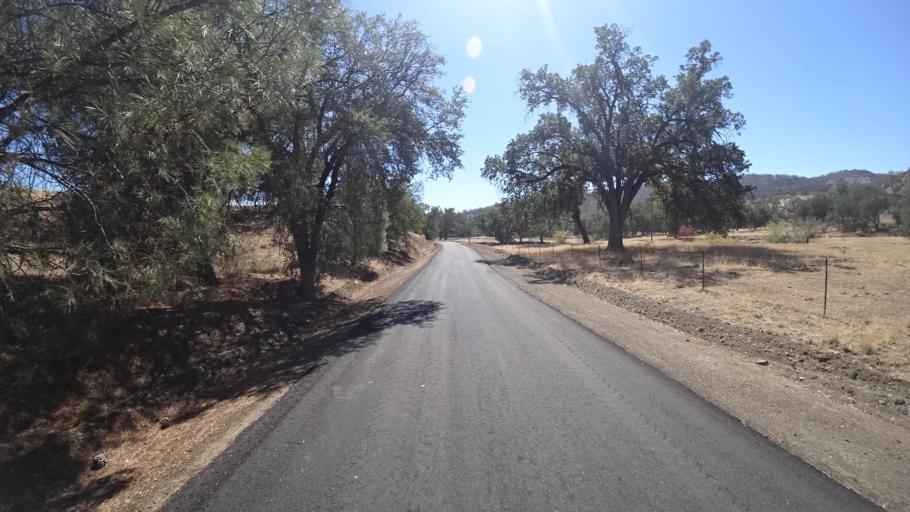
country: US
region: California
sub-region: Fresno County
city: Coalinga
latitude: 35.9354
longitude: -120.4589
